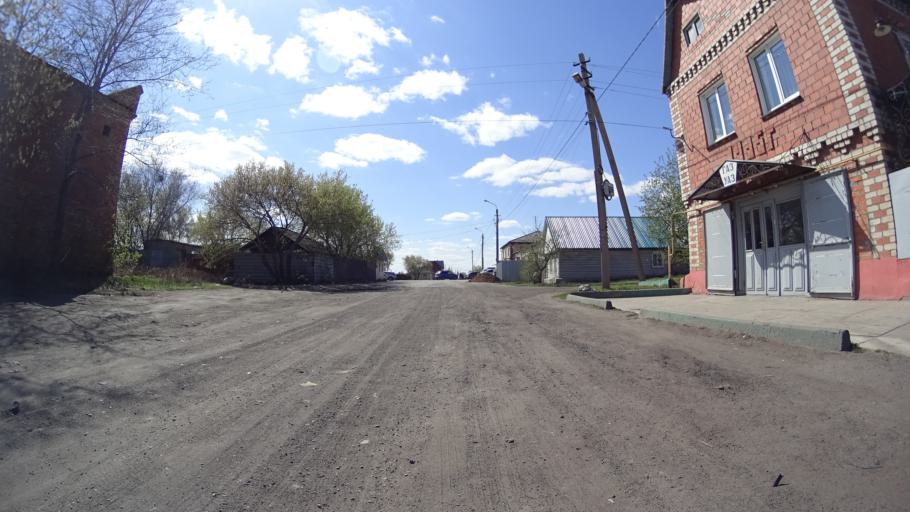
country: RU
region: Chelyabinsk
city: Troitsk
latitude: 54.0937
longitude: 61.5940
